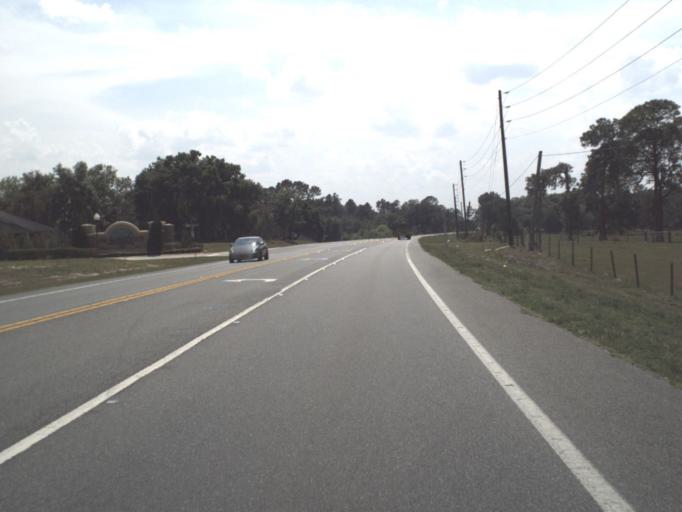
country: US
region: Florida
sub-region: Lake County
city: Howie In The Hills
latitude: 28.6611
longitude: -81.7849
